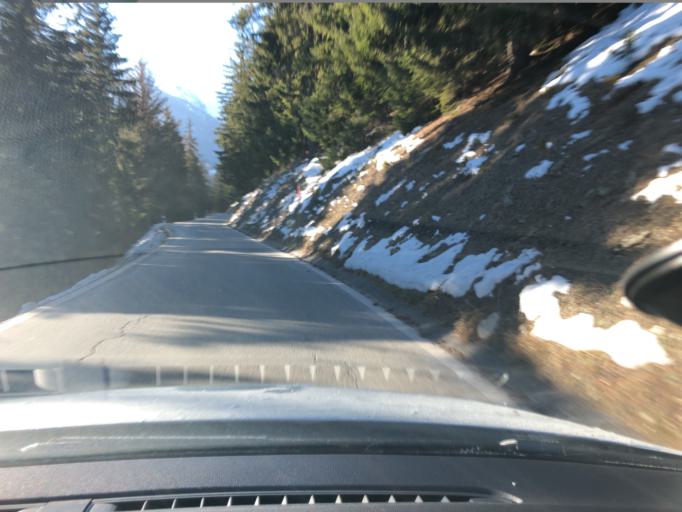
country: CH
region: Valais
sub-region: Goms District
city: Fiesch
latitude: 46.4113
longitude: 8.1474
